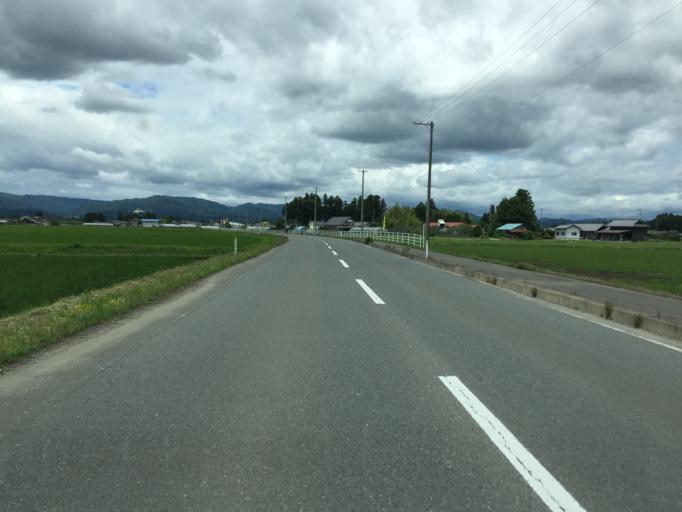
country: JP
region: Fukushima
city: Namie
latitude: 37.6470
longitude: 140.9957
